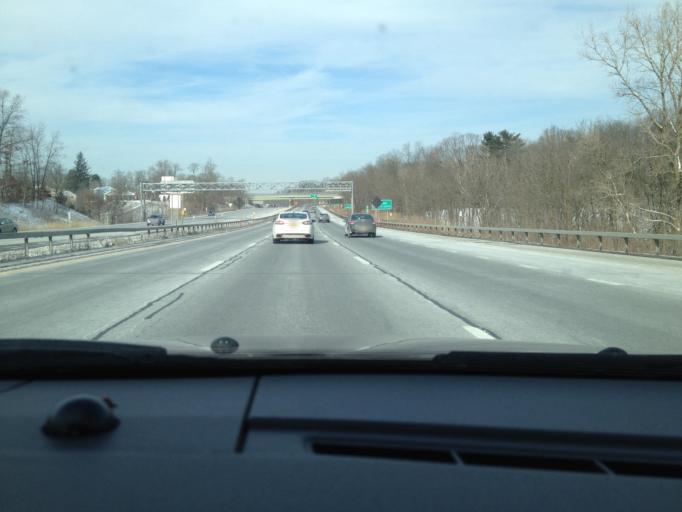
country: US
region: New York
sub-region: Rensselaer County
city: Rensselaer
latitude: 42.6566
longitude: -73.7192
